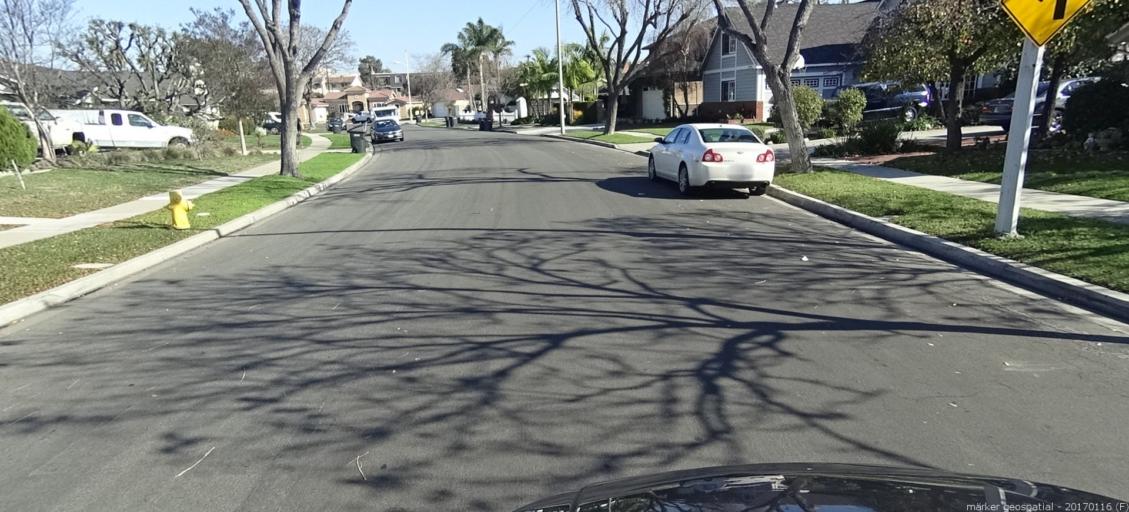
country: US
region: California
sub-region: Orange County
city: Rossmoor
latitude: 33.7831
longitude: -118.0785
